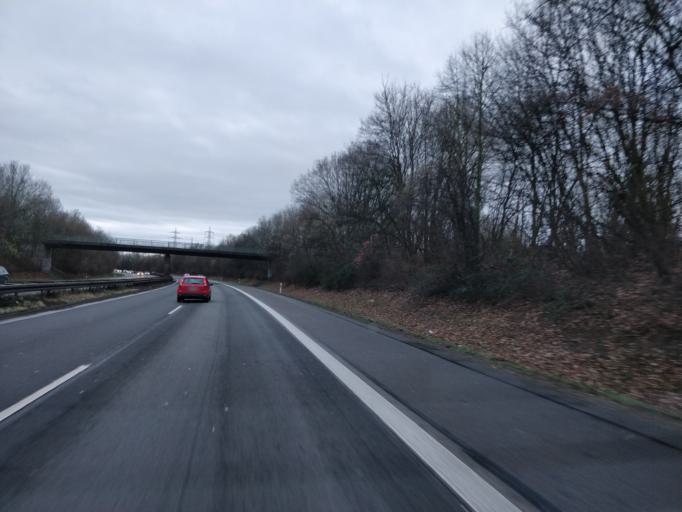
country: DE
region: North Rhine-Westphalia
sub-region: Regierungsbezirk Koln
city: Wahn-Heide
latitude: 50.8320
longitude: 7.0938
